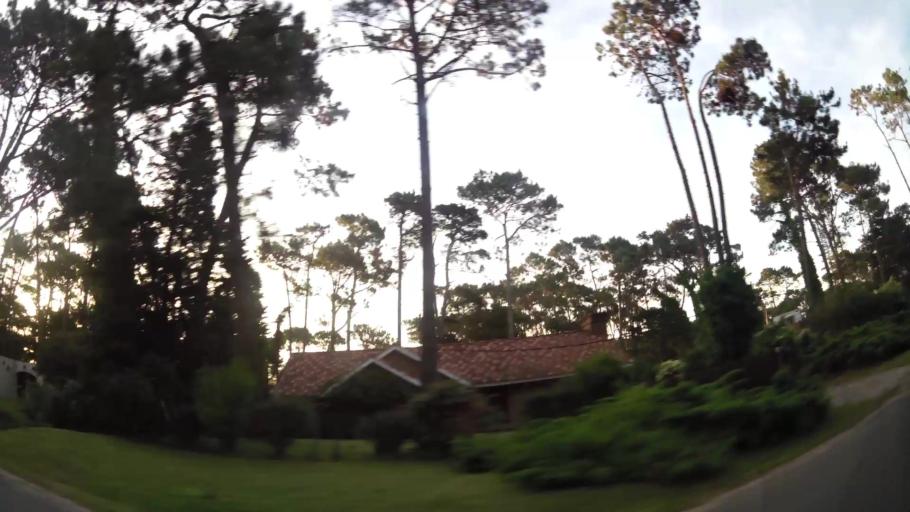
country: UY
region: Maldonado
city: Maldonado
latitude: -34.9324
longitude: -54.9352
